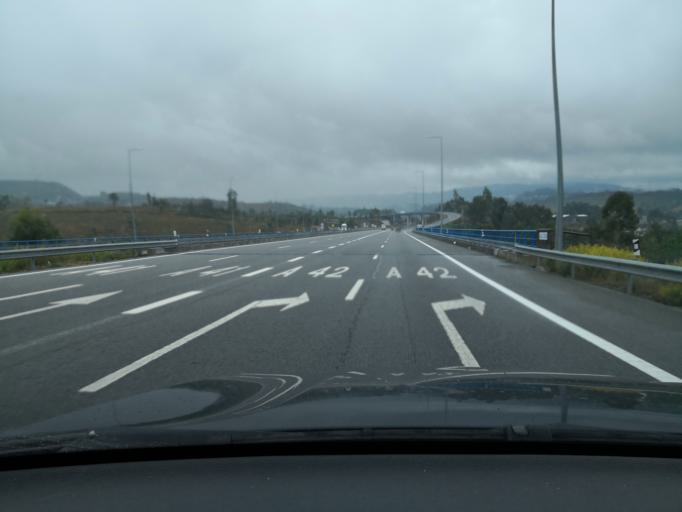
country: PT
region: Porto
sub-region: Valongo
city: Sobrado
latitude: 41.2316
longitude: -8.4627
